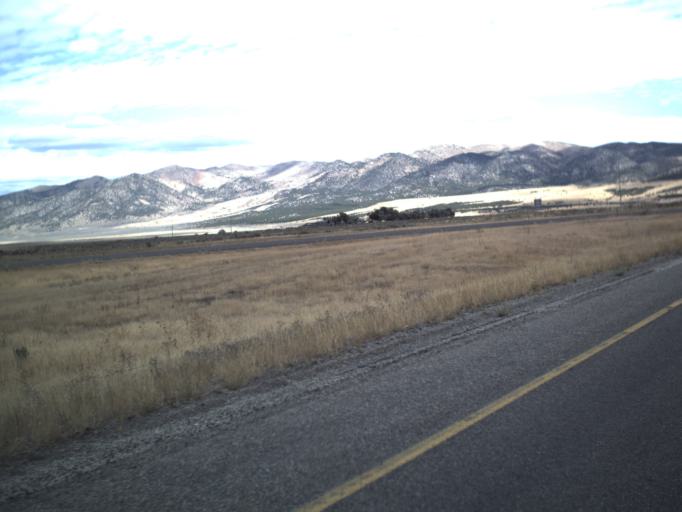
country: US
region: Idaho
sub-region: Oneida County
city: Malad City
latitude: 41.9604
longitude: -112.7080
